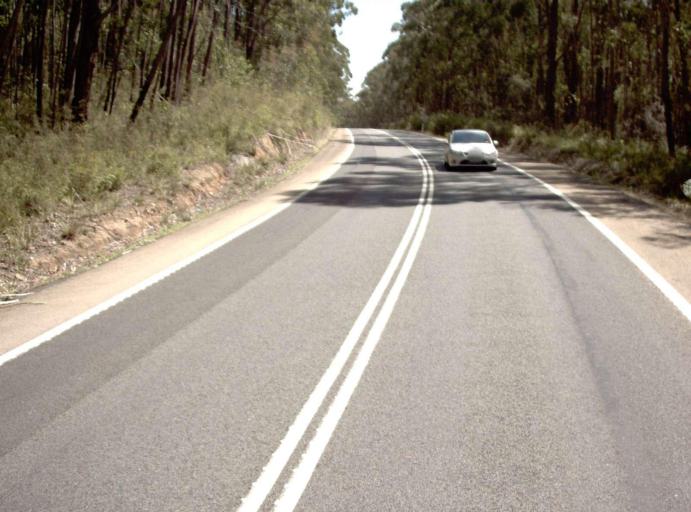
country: AU
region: New South Wales
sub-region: Bombala
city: Bombala
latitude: -37.5649
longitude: 149.3276
